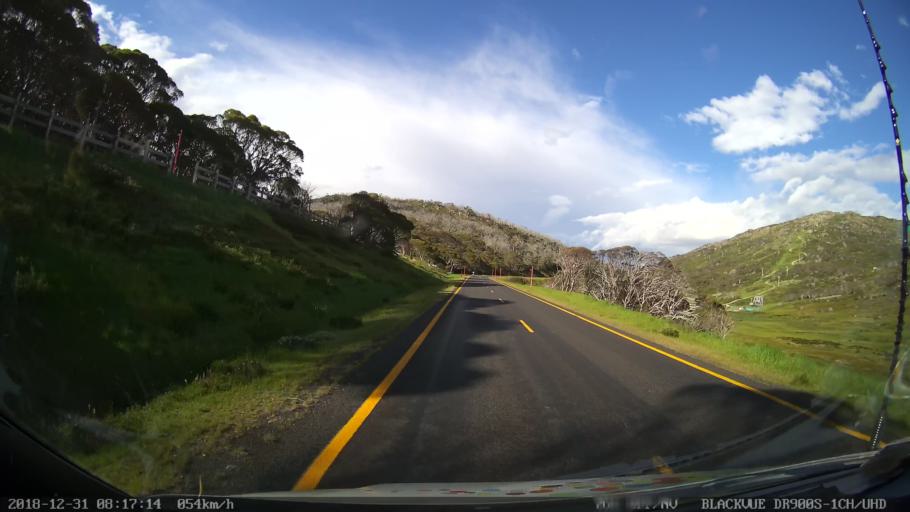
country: AU
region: New South Wales
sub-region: Snowy River
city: Jindabyne
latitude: -36.4094
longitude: 148.4061
